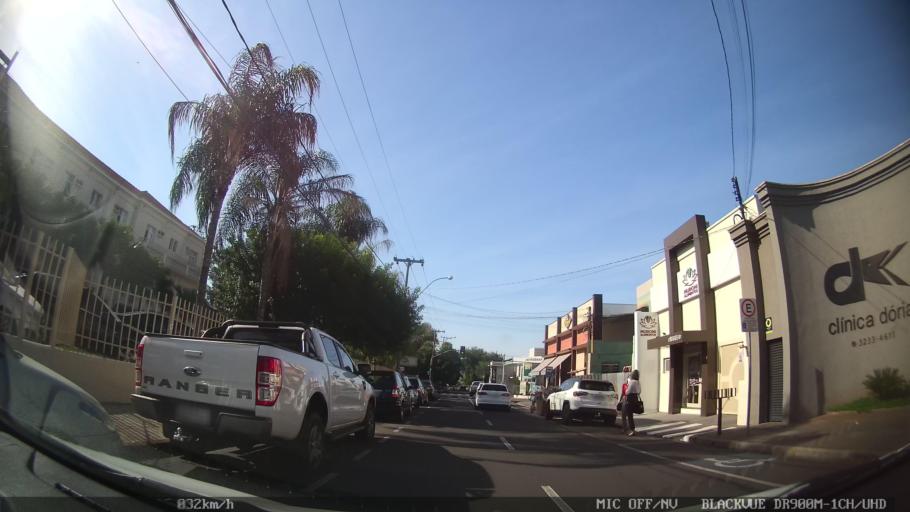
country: BR
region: Sao Paulo
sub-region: Sao Jose Do Rio Preto
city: Sao Jose do Rio Preto
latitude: -20.8038
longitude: -49.3861
